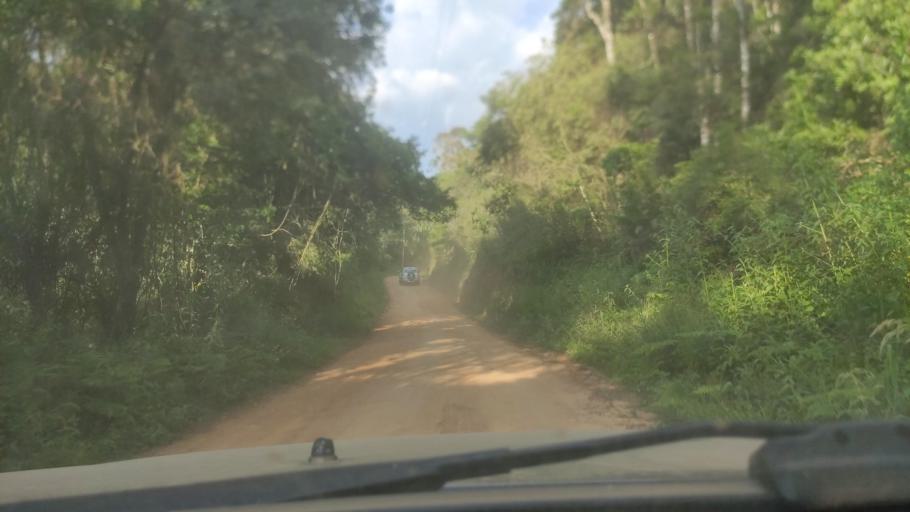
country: BR
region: Minas Gerais
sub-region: Cambui
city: Cambui
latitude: -22.7563
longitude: -45.9488
